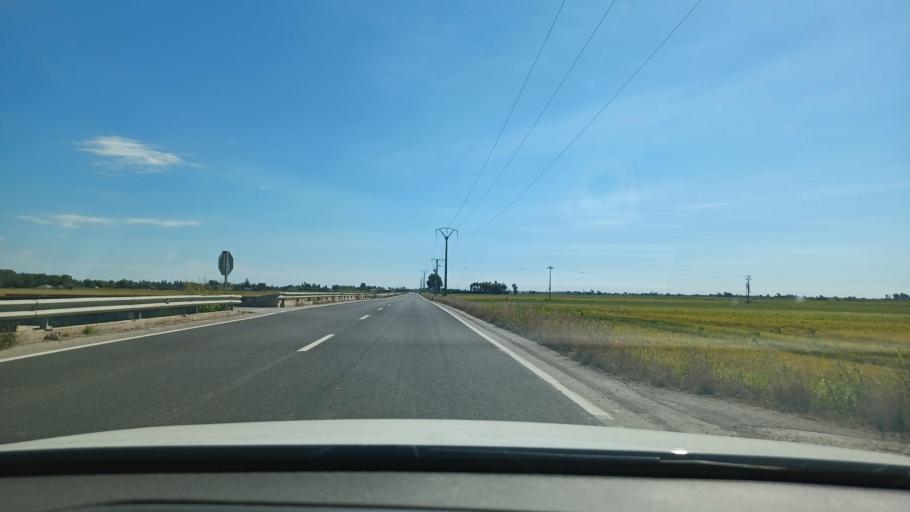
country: ES
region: Catalonia
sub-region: Provincia de Tarragona
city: Deltebre
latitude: 40.7106
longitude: 0.6659
